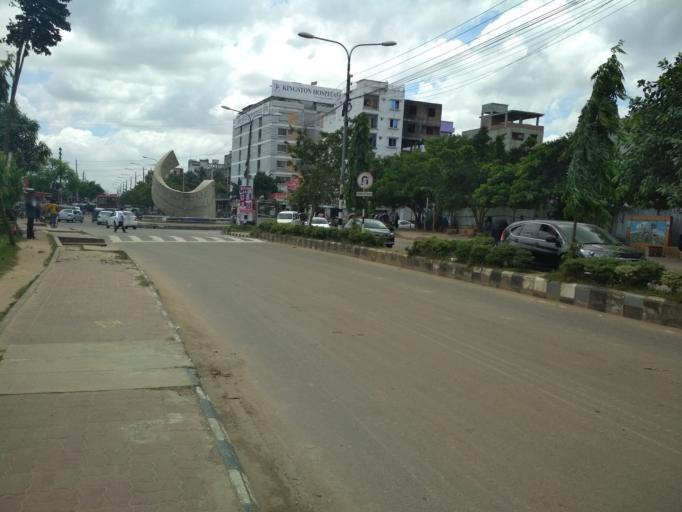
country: BD
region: Dhaka
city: Tungi
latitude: 23.8308
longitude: 90.3767
